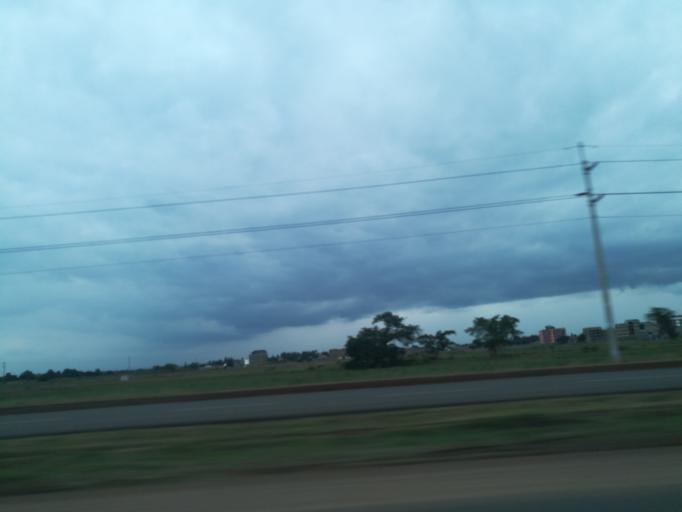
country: KE
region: Nairobi Area
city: Thika
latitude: -1.0486
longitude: 37.0587
